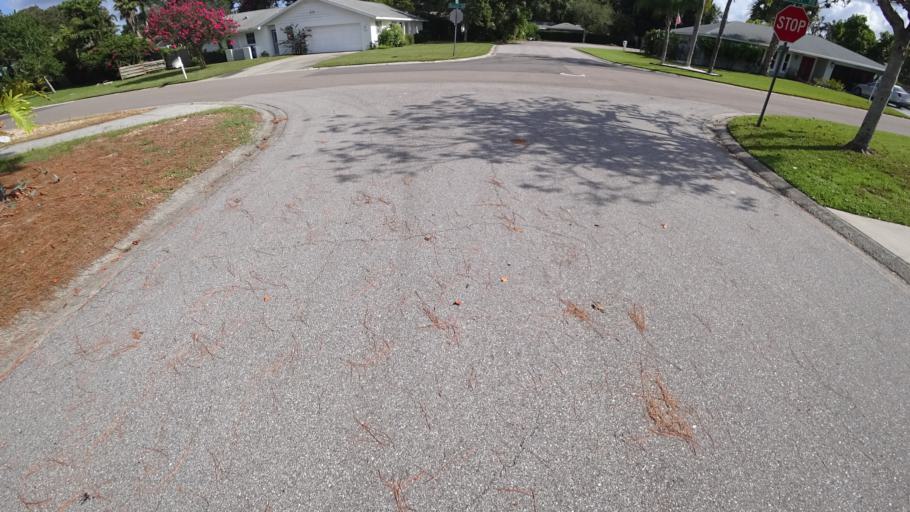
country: US
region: Florida
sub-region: Sarasota County
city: Desoto Lakes
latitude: 27.4033
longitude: -82.4977
